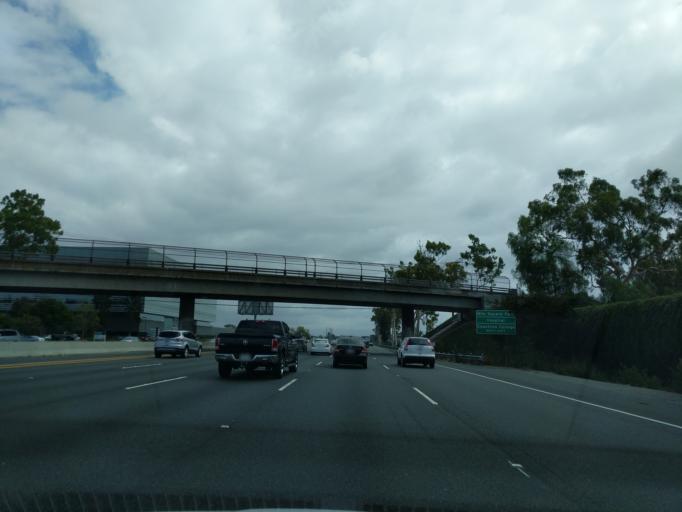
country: US
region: California
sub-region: Orange County
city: Fountain Valley
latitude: 33.7001
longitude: -117.9462
